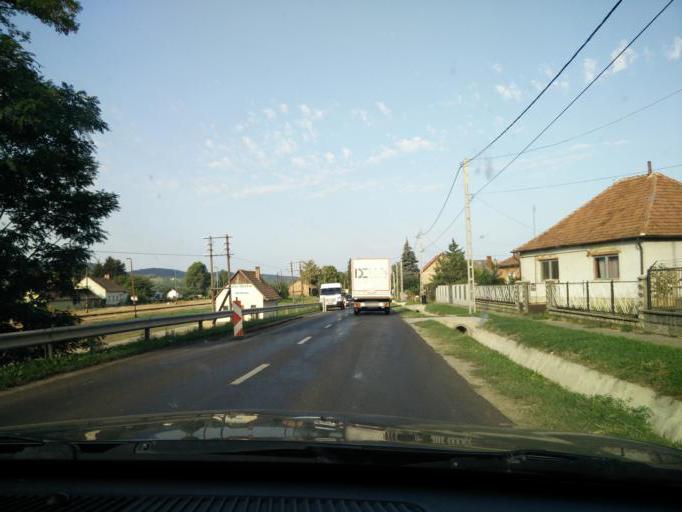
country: HU
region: Baranya
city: Szaszvar
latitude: 46.2799
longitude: 18.4128
